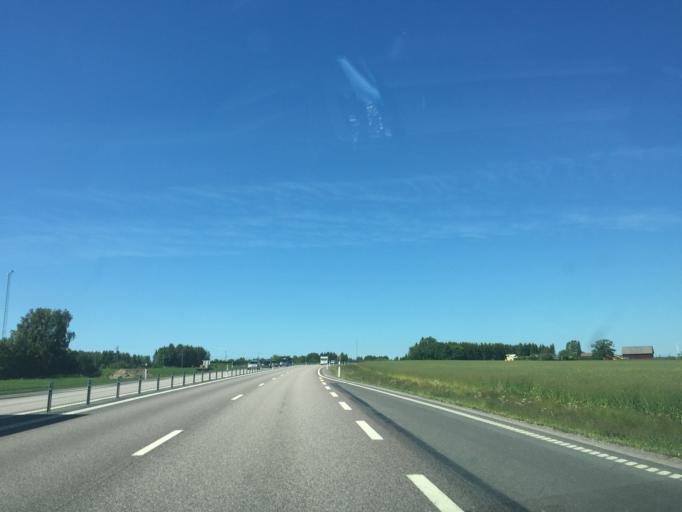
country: SE
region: OEstergoetland
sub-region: Motala Kommun
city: Stenstorp
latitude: 58.4059
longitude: 15.0855
